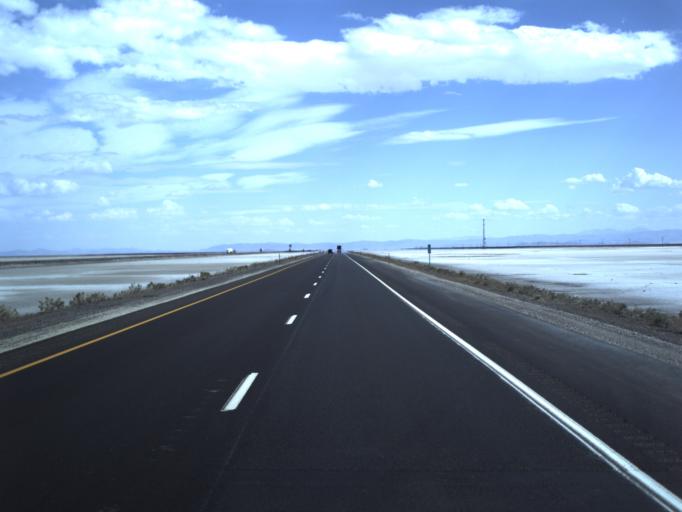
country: US
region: Utah
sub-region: Tooele County
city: Wendover
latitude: 40.7329
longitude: -113.5897
